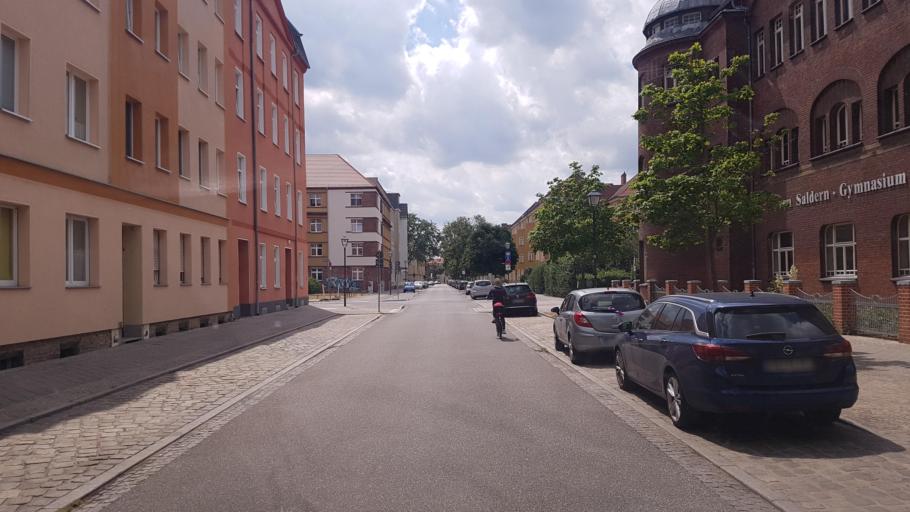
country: DE
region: Brandenburg
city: Brandenburg an der Havel
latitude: 52.4032
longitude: 12.5489
